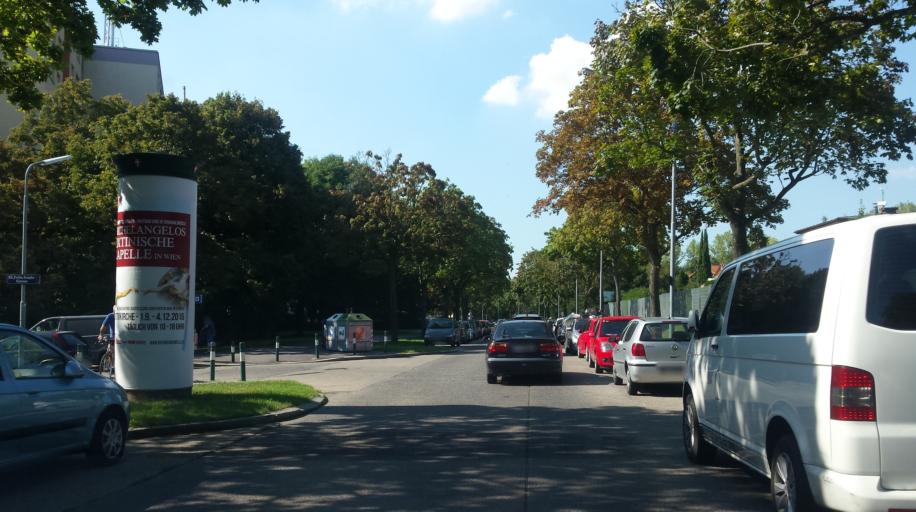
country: AT
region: Lower Austria
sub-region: Politischer Bezirk Wien-Umgebung
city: Leopoldsdorf
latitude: 48.1516
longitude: 16.3883
